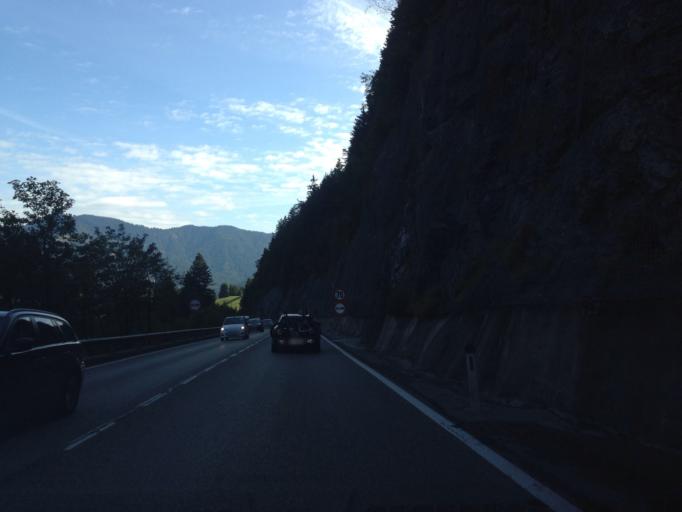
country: AT
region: Tyrol
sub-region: Politischer Bezirk Reutte
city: Reutte
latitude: 47.4647
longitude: 10.7212
